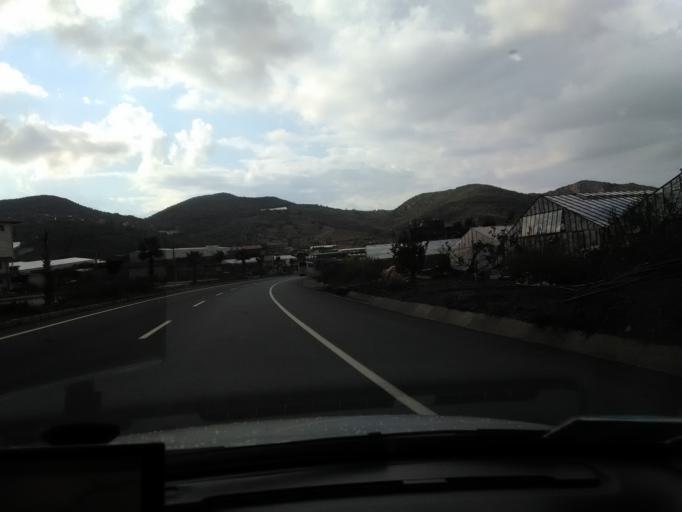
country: TR
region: Antalya
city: Gazipasa
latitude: 36.1906
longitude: 32.4090
